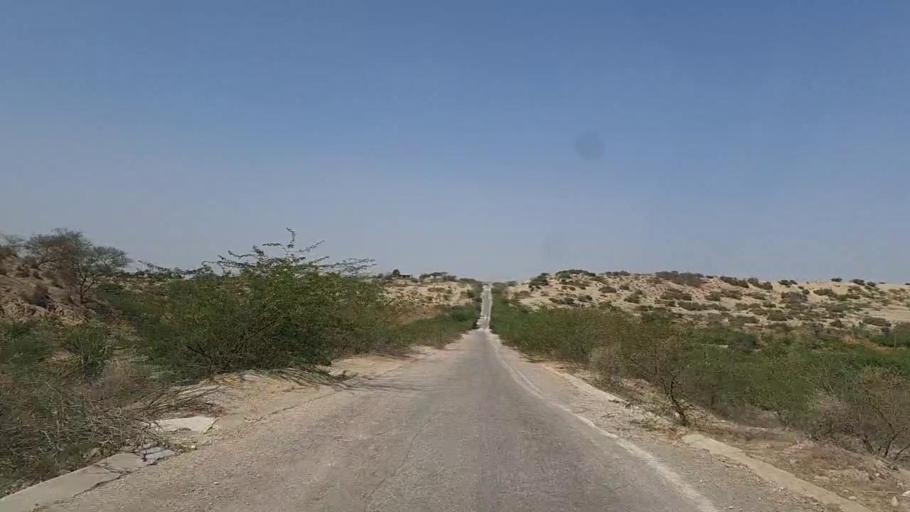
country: PK
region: Sindh
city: Naukot
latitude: 24.5854
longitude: 69.3182
